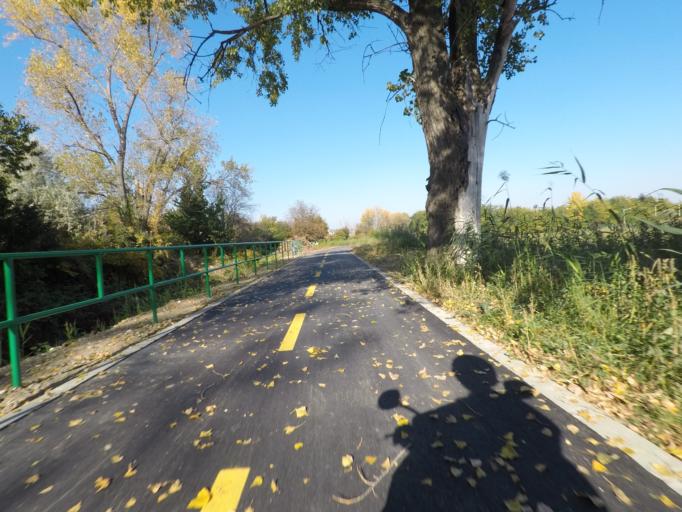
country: HU
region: Pest
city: Pomaz
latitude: 47.6442
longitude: 19.0408
